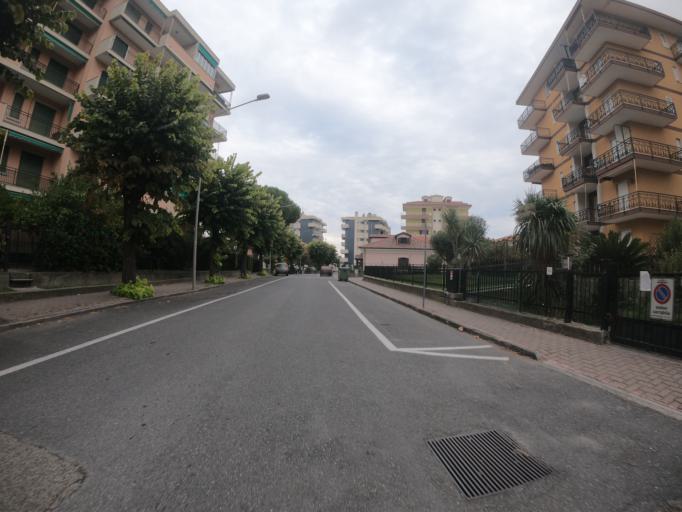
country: IT
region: Liguria
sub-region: Provincia di Savona
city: Marina di Andora
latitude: 43.9527
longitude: 8.1484
